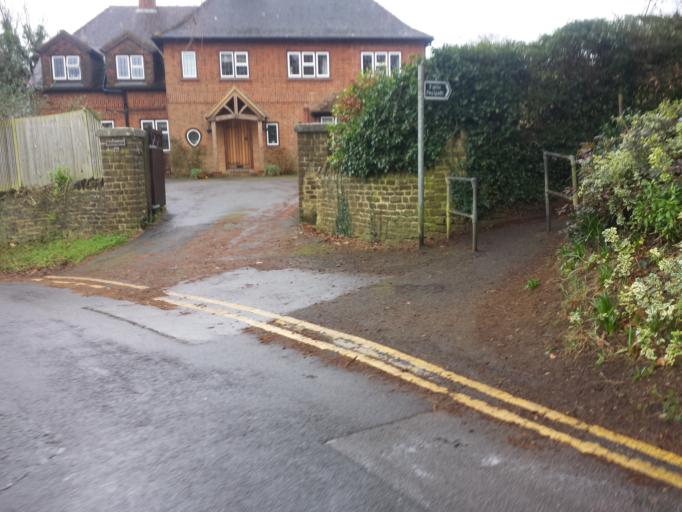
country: GB
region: England
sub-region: Surrey
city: Godalming
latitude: 51.1789
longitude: -0.6081
